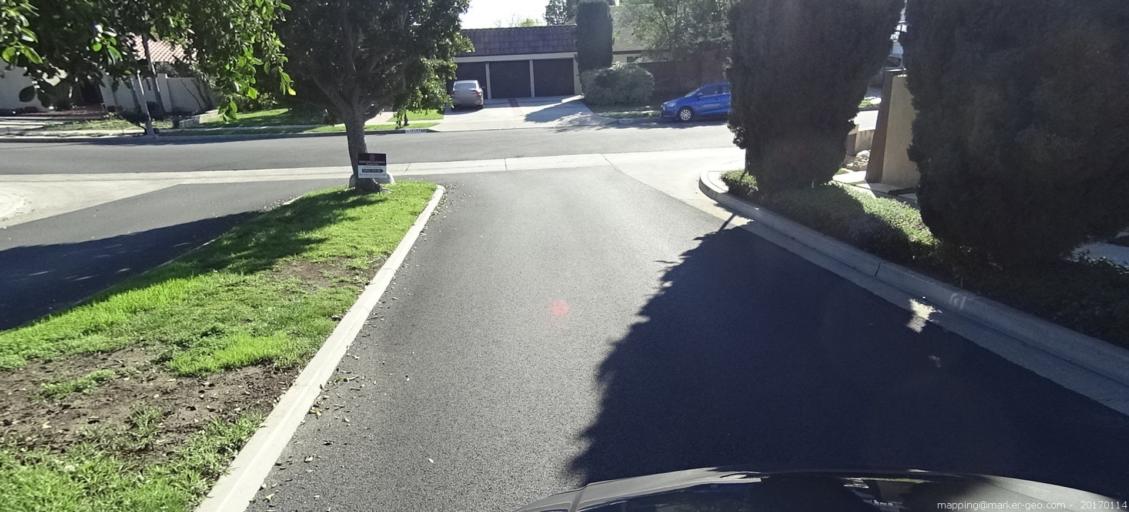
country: US
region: California
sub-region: Orange County
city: North Tustin
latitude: 33.7732
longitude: -117.8176
